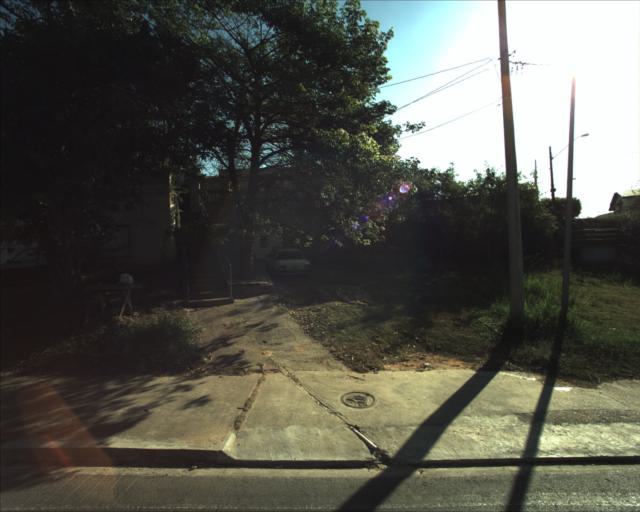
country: BR
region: Sao Paulo
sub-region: Sorocaba
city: Sorocaba
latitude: -23.4751
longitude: -47.4429
